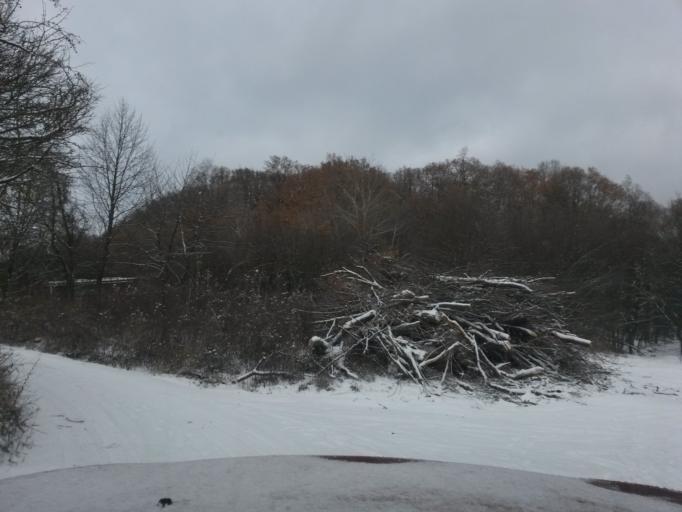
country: HU
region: Borsod-Abauj-Zemplen
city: Gonc
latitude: 48.5978
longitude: 21.3900
